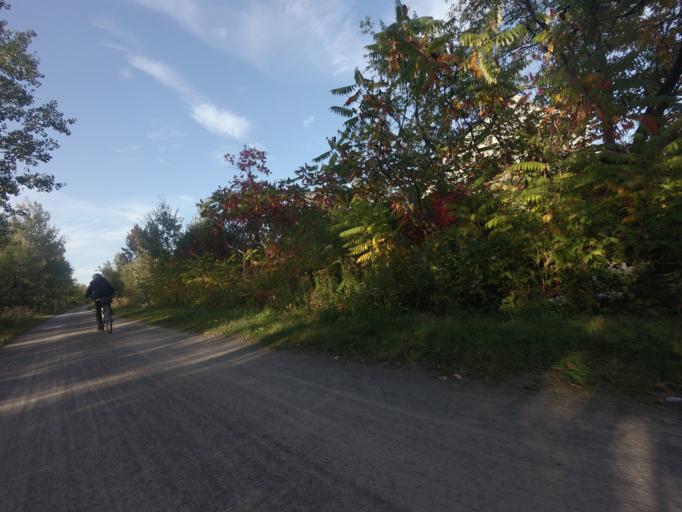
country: CA
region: Quebec
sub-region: Laurentides
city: Prevost
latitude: 45.8370
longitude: -74.0589
